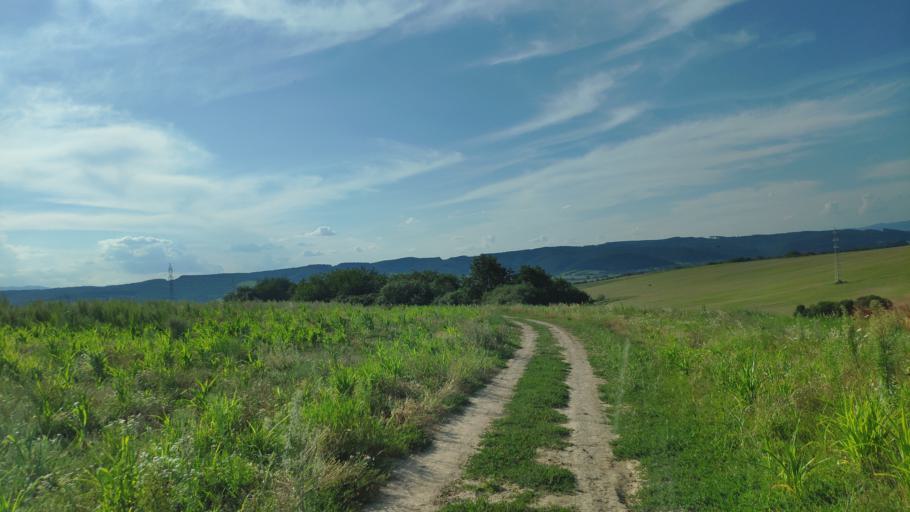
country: SK
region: Presovsky
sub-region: Okres Presov
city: Presov
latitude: 48.9131
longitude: 21.2747
